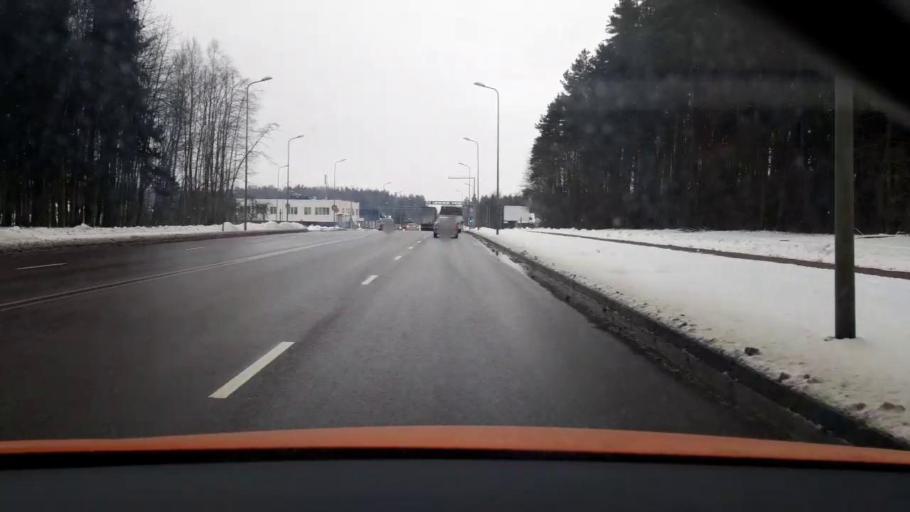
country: LT
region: Vilnius County
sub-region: Vilnius
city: Fabijoniskes
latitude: 54.7632
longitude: 25.2718
